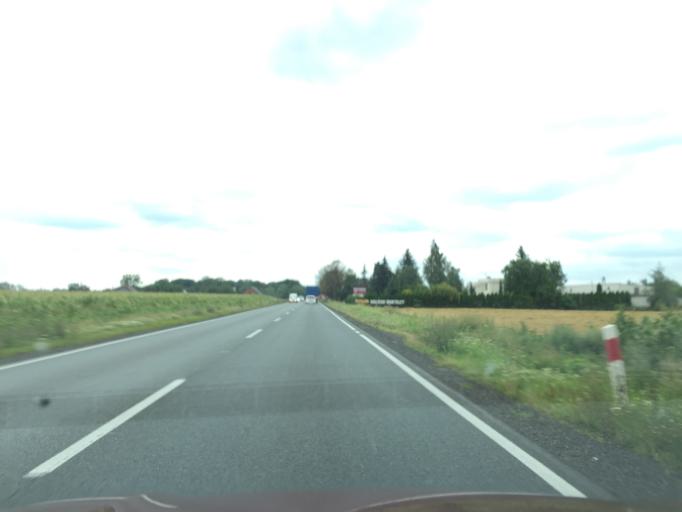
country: PL
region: Greater Poland Voivodeship
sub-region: Kalisz
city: Kalisz
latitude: 51.8195
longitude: 18.0934
